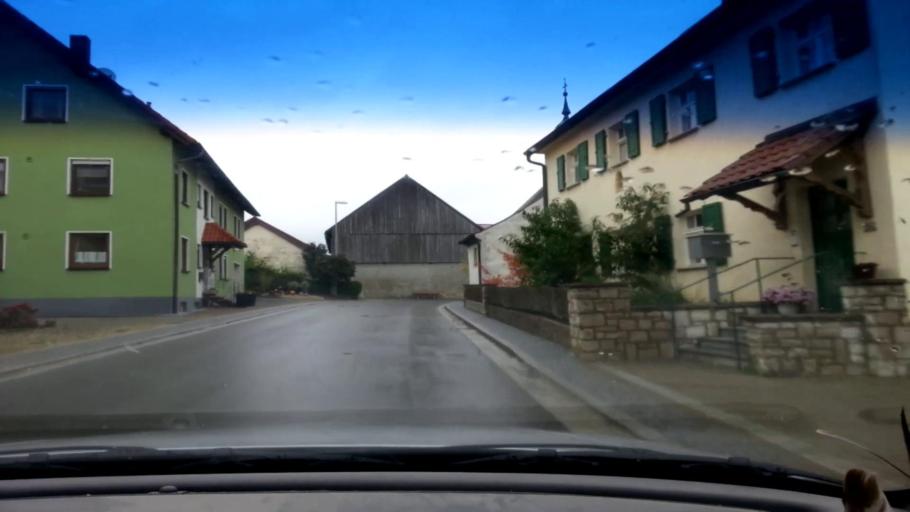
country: DE
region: Bavaria
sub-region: Upper Franconia
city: Poxdorf
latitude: 49.9630
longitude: 11.0996
